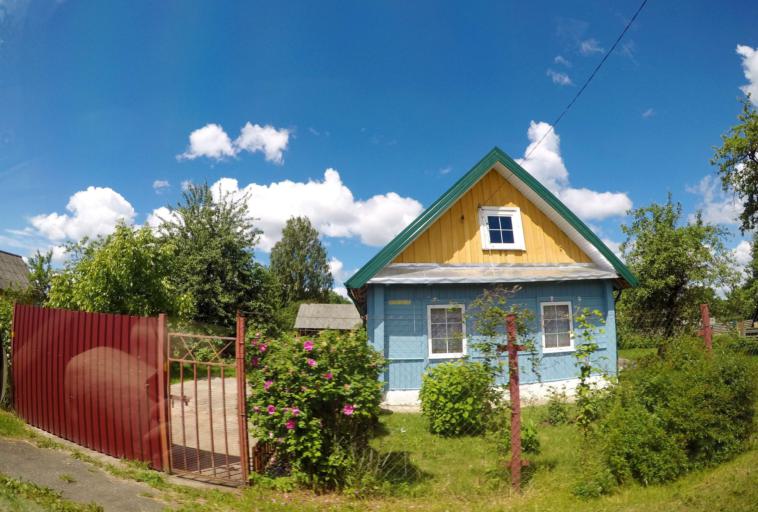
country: BY
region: Grodnenskaya
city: Hal'shany
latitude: 54.1649
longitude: 26.0913
